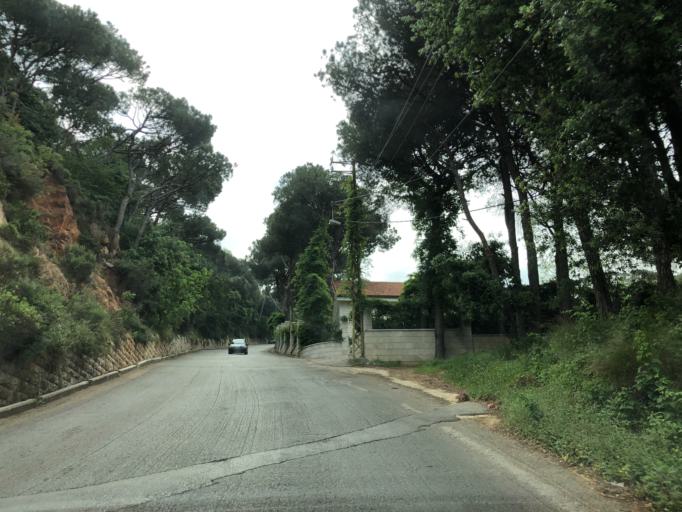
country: LB
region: Mont-Liban
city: Jdaidet el Matn
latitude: 33.8596
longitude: 35.5991
